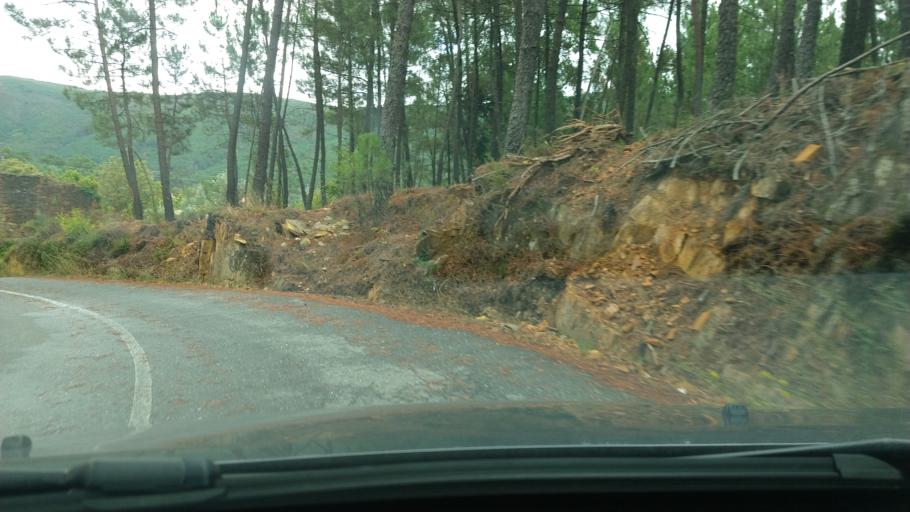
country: PT
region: Castelo Branco
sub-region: Concelho do Fundao
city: Aldeia de Joanes
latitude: 40.2186
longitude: -7.6300
